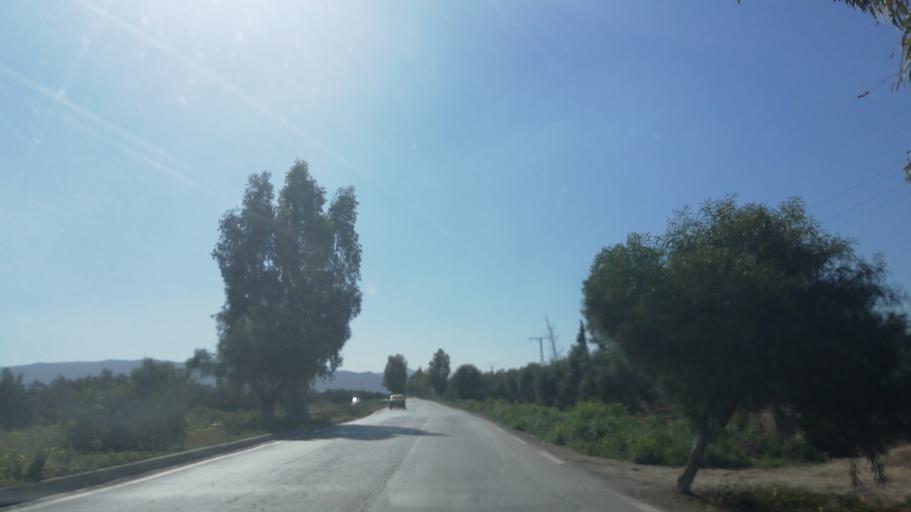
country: DZ
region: Mascara
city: Sig
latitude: 35.5551
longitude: -0.2069
